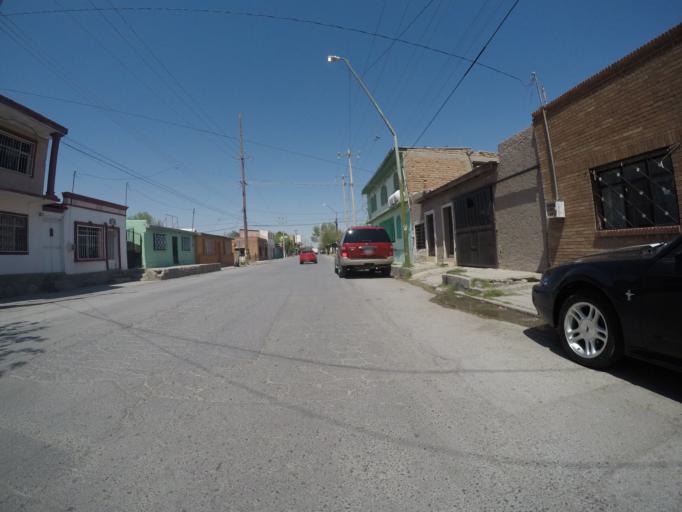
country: MX
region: Chihuahua
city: Ciudad Juarez
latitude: 31.7267
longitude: -106.4801
